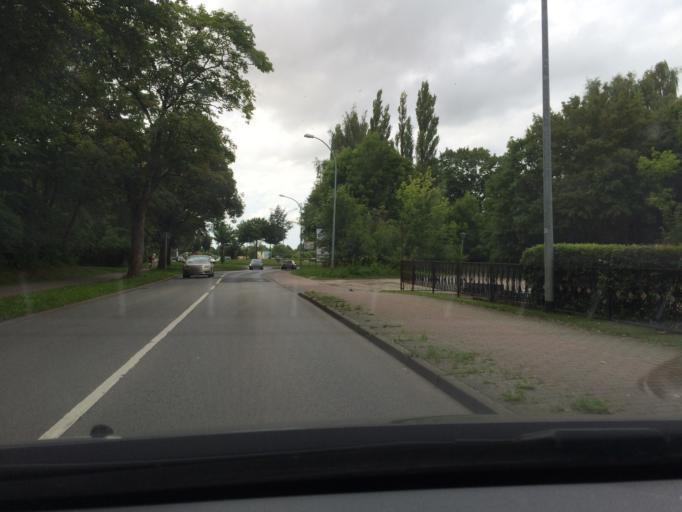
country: DE
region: Mecklenburg-Vorpommern
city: Kramerhof
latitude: 54.3330
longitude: 13.0658
